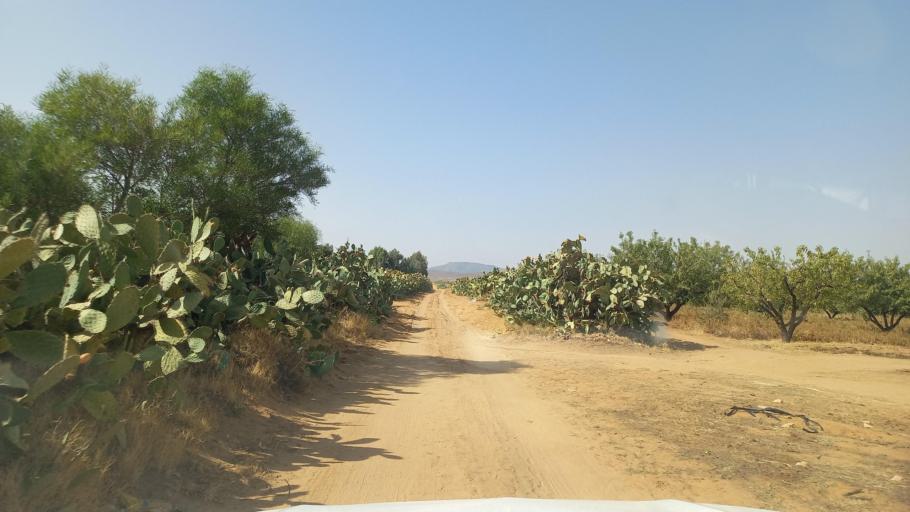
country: TN
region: Al Qasrayn
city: Kasserine
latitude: 35.2351
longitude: 9.0543
